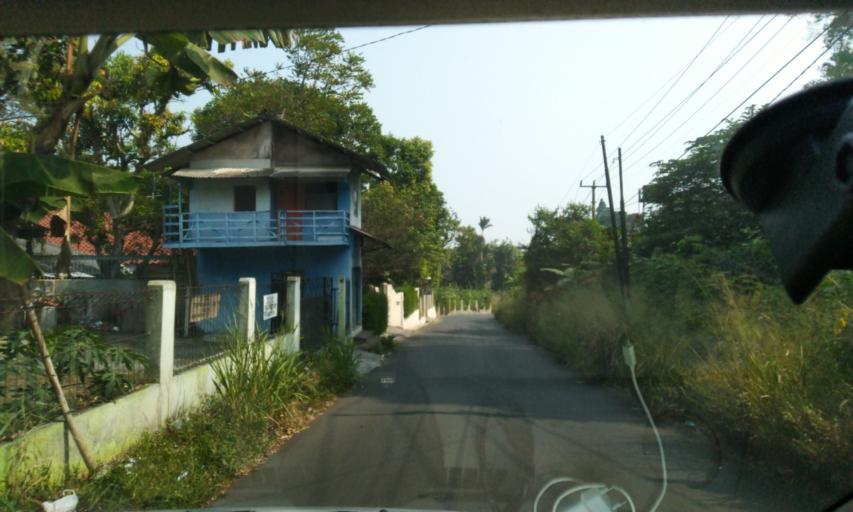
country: ID
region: West Java
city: Caringin
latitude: -6.6654
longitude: 106.8635
